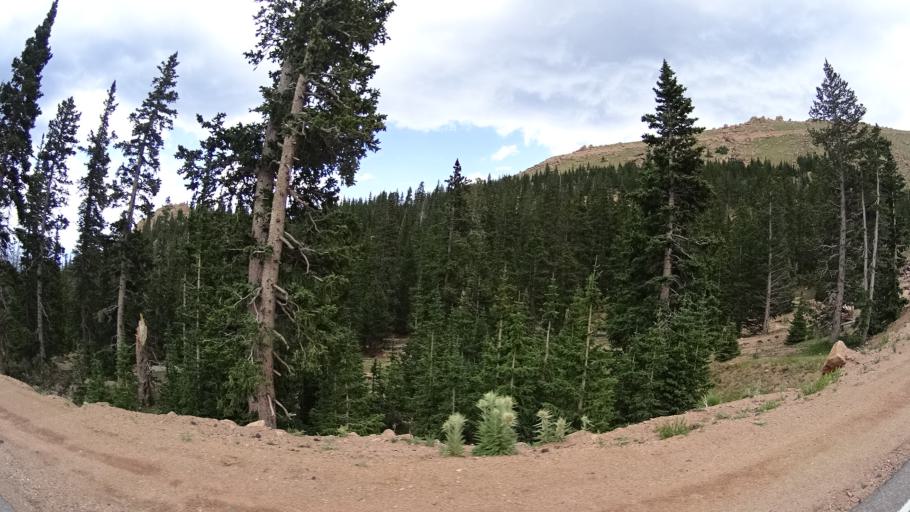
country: US
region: Colorado
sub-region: El Paso County
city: Cascade-Chipita Park
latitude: 38.8728
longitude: -105.0717
